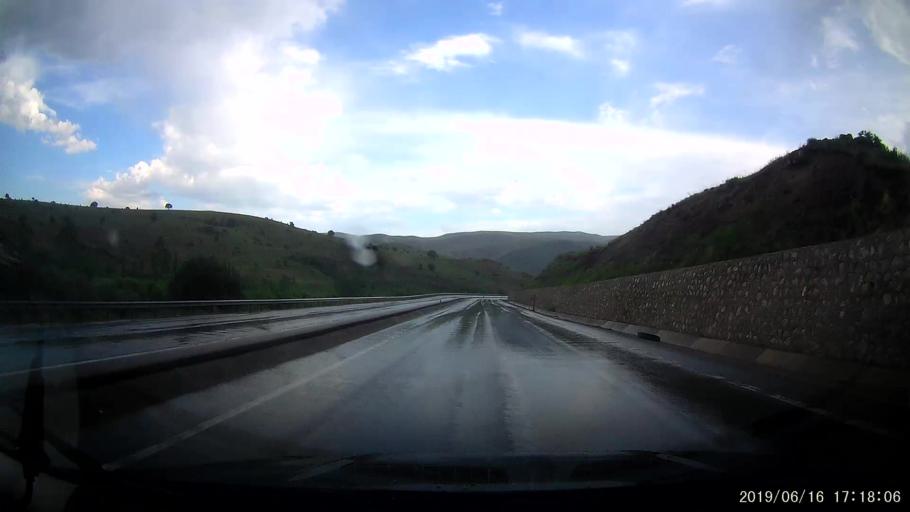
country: TR
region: Erzincan
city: Tercan
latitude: 39.8185
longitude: 40.5288
